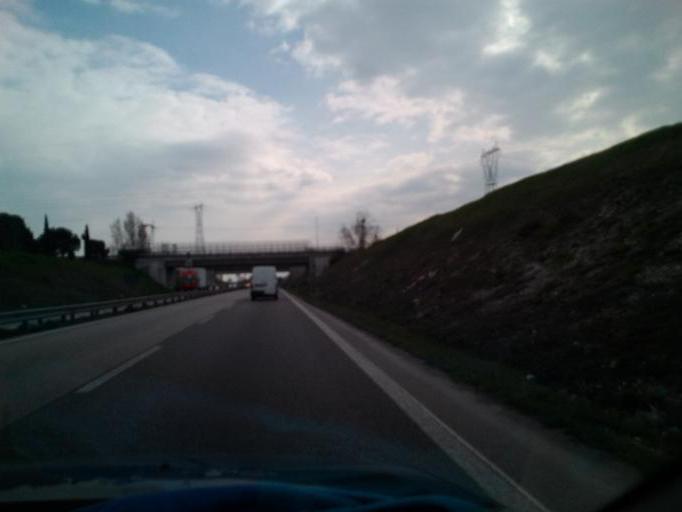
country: IT
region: Veneto
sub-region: Provincia di Verona
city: Caselle
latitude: 45.4257
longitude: 10.9148
